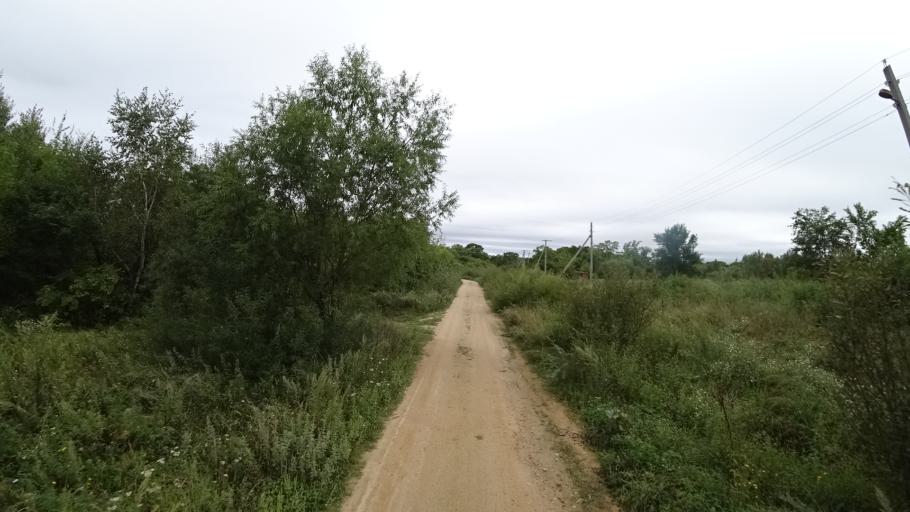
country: RU
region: Primorskiy
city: Rettikhovka
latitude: 44.1382
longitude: 132.6376
